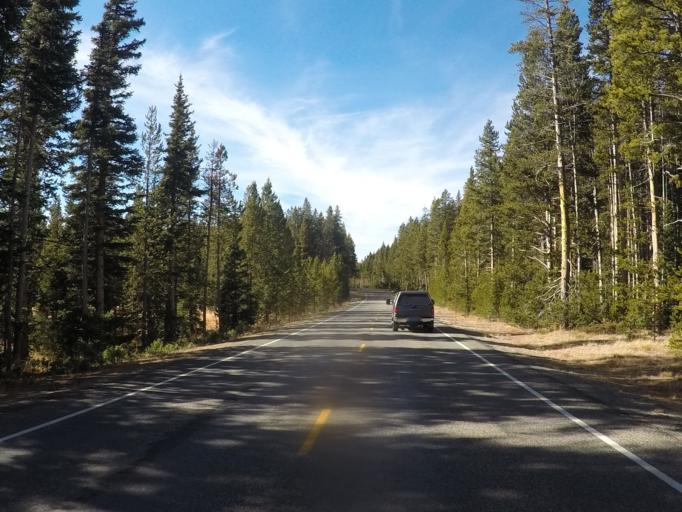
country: US
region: Montana
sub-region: Gallatin County
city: West Yellowstone
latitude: 44.4575
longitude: -110.4888
